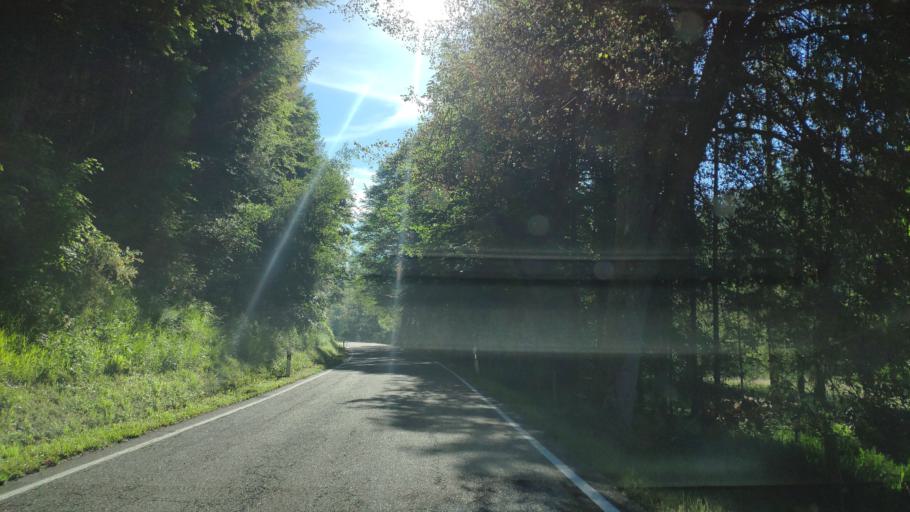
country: DE
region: Rheinland-Pfalz
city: Bundenthal
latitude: 49.0851
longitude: 7.8268
